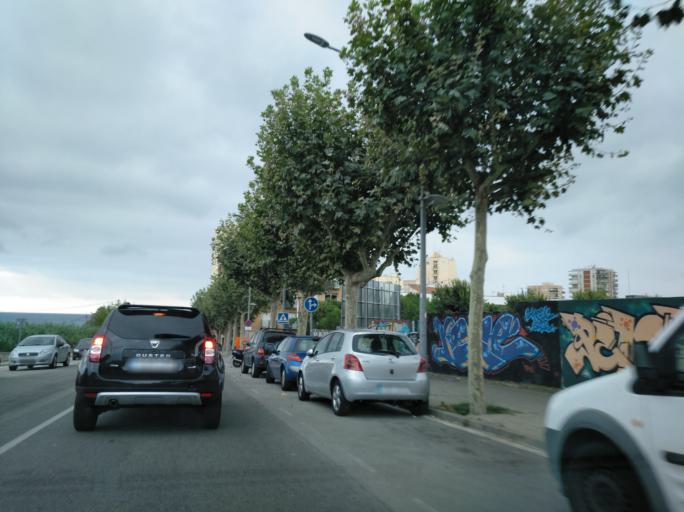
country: ES
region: Catalonia
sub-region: Provincia de Barcelona
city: Mataro
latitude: 41.5427
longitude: 2.4554
